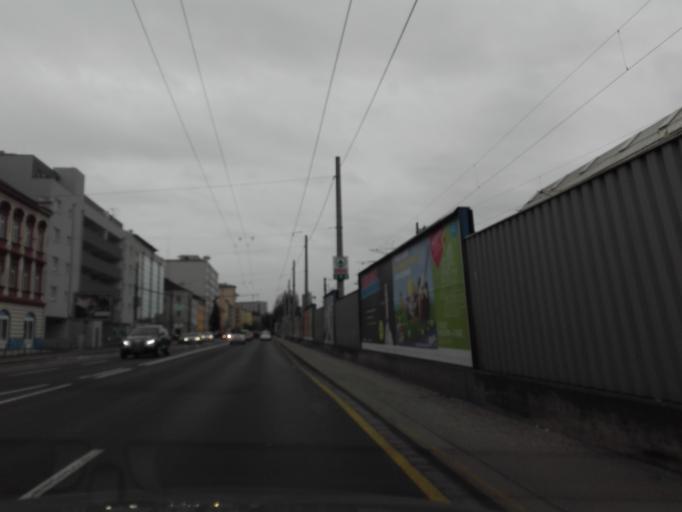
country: AT
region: Upper Austria
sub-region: Linz Stadt
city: Linz
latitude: 48.2894
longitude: 14.2966
